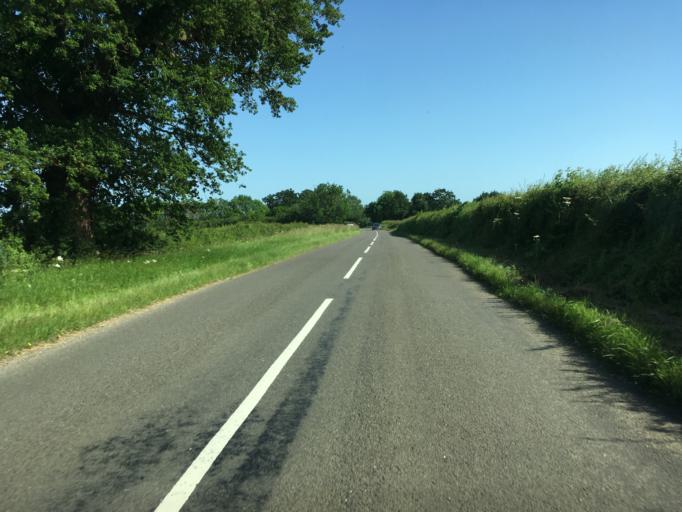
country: GB
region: England
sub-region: Buckinghamshire
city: Steeple Claydon
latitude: 51.9410
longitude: -0.9450
